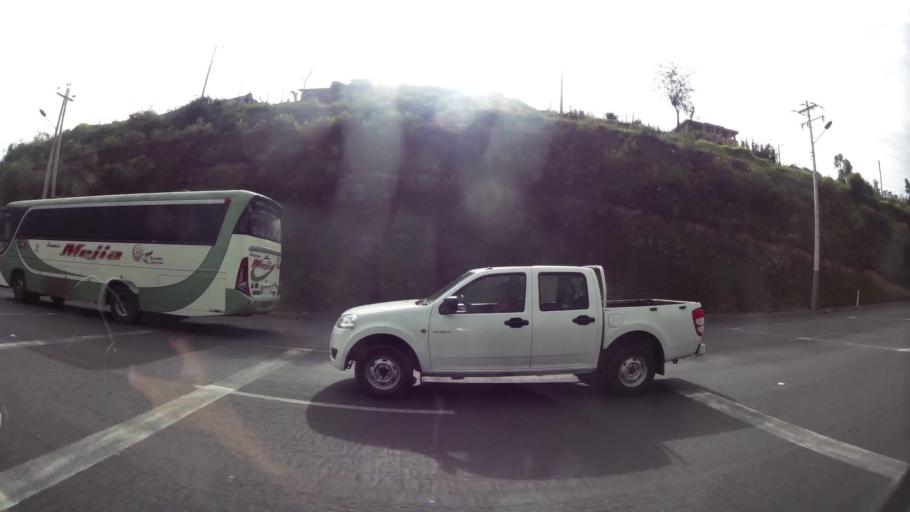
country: EC
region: Pichincha
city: Sangolqui
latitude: -0.4003
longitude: -78.5416
